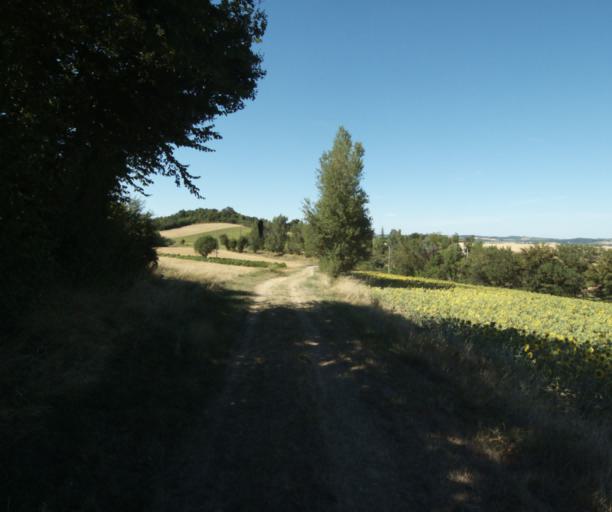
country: FR
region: Midi-Pyrenees
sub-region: Departement de la Haute-Garonne
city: Saint-Felix-Lauragais
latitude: 43.5167
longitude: 1.9295
